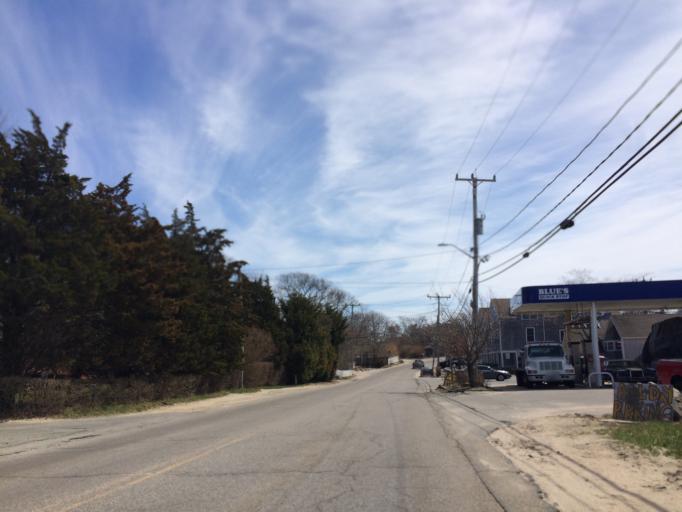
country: US
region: Massachusetts
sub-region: Barnstable County
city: Provincetown
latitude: 42.0585
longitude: -70.1884
